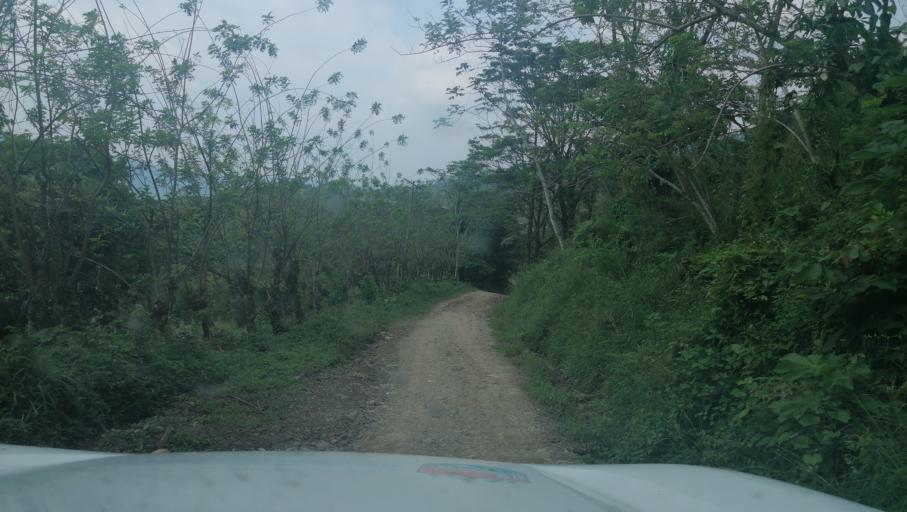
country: MX
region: Chiapas
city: Ostuacan
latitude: 17.3596
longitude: -93.3242
